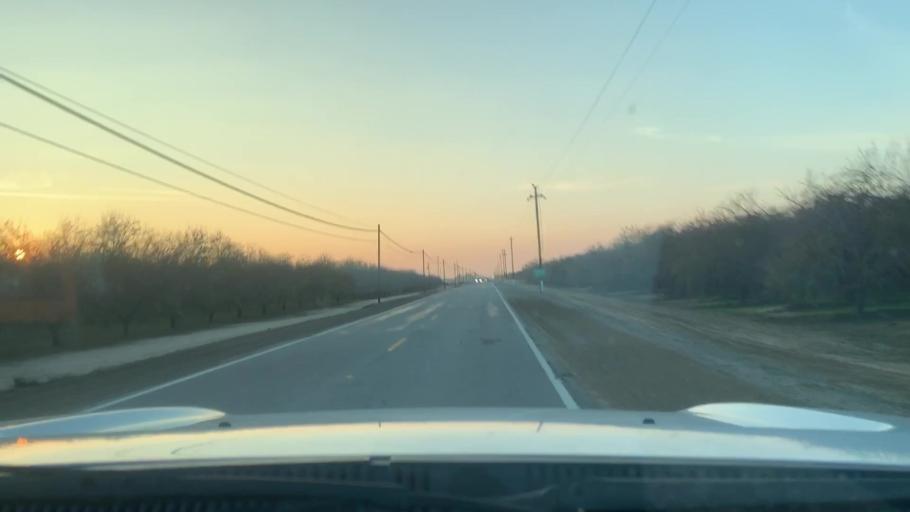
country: US
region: California
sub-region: Kern County
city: Rosedale
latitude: 35.3835
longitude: -119.2312
